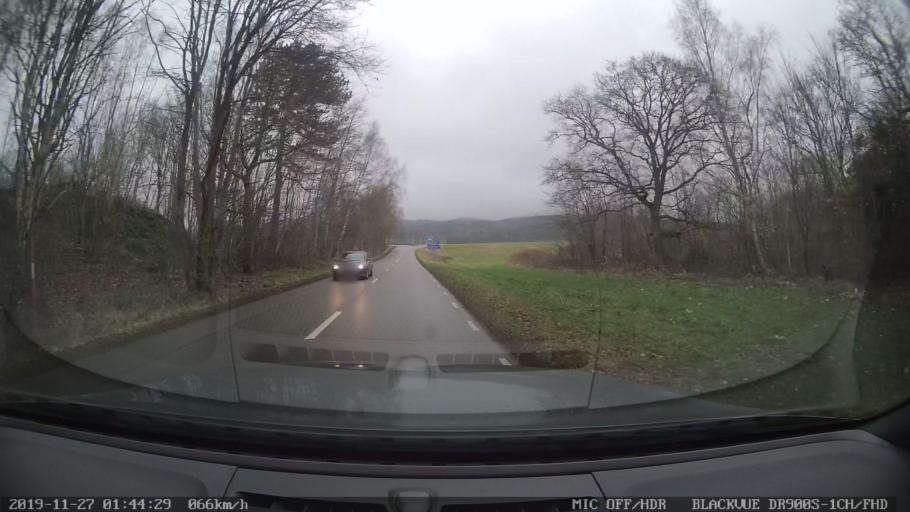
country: SE
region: Skane
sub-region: Hoganas Kommun
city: Hoganas
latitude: 56.2689
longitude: 12.5328
